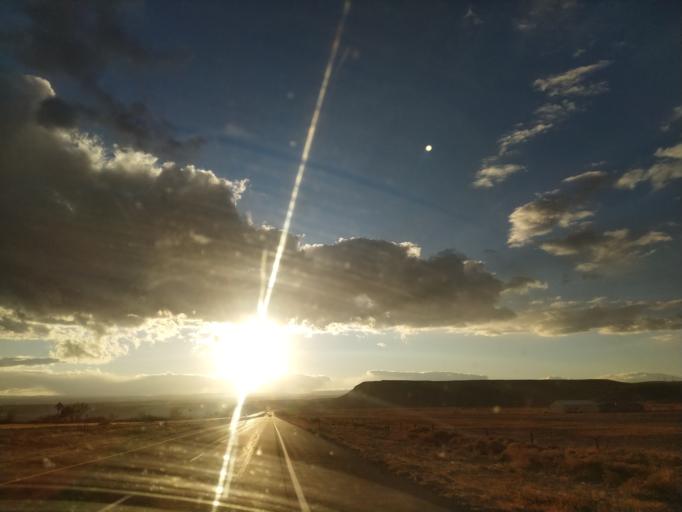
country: US
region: Colorado
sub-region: Delta County
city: Delta
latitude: 38.7575
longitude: -108.1456
